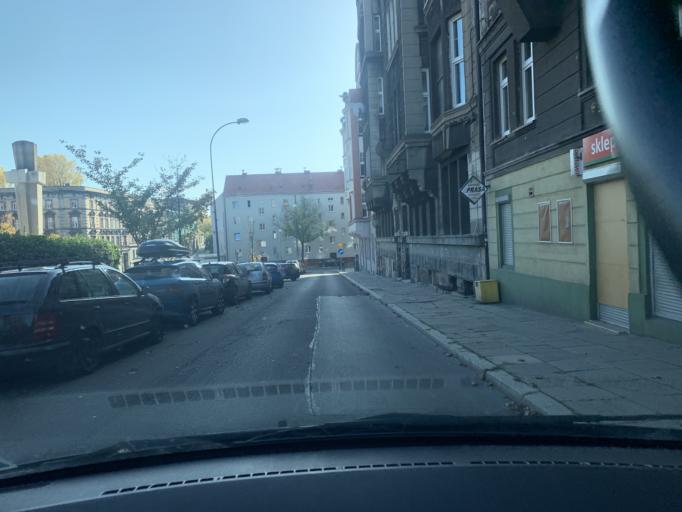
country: PL
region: Silesian Voivodeship
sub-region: Bytom
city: Bytom
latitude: 50.3519
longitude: 18.9165
